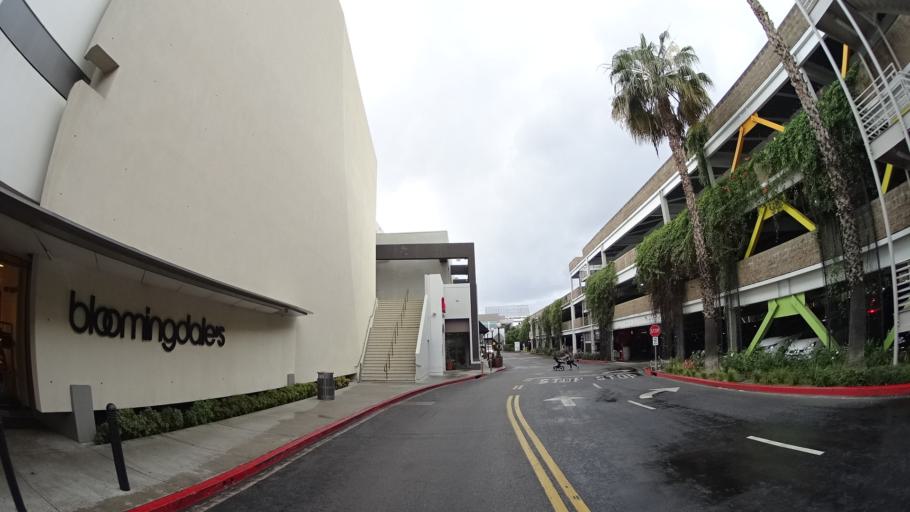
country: US
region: California
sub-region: Los Angeles County
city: Sherman Oaks
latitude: 34.1565
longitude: -118.4392
